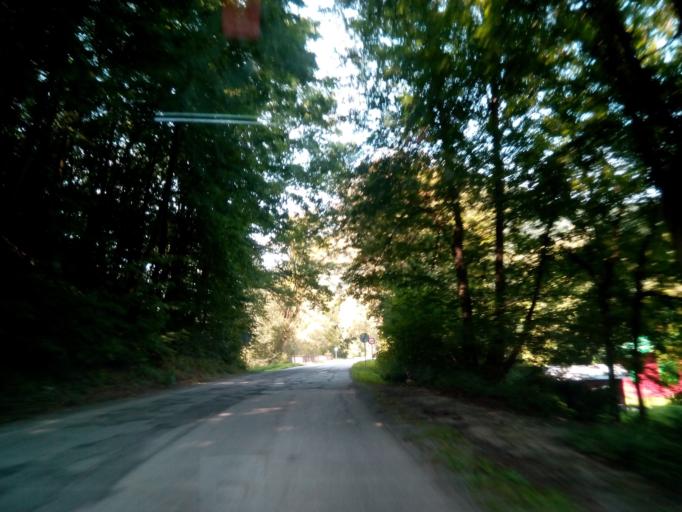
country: SK
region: Presovsky
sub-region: Okres Presov
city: Presov
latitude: 48.8572
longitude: 21.1883
